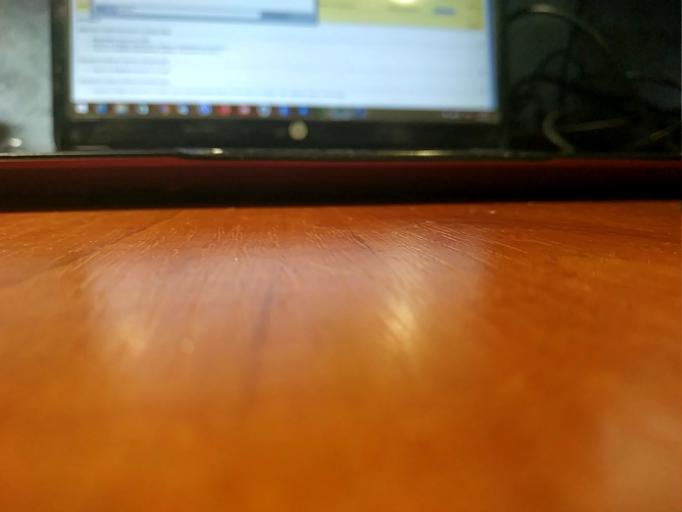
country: RU
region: Vologda
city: Ustyuzhna
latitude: 58.6625
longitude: 36.4250
